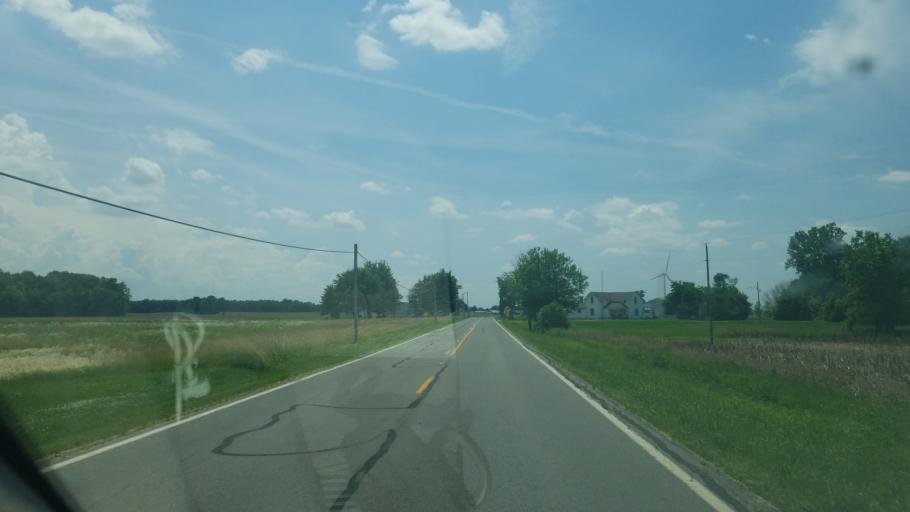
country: US
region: Ohio
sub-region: Hardin County
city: Ada
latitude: 40.7784
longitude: -83.7012
